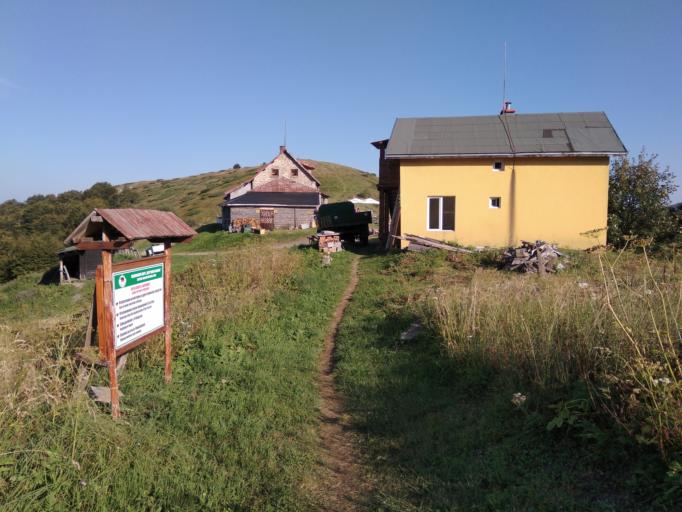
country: BG
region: Stara Zagora
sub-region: Obshtina Pavel Banya
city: Asen
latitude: 42.7589
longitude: 25.1139
